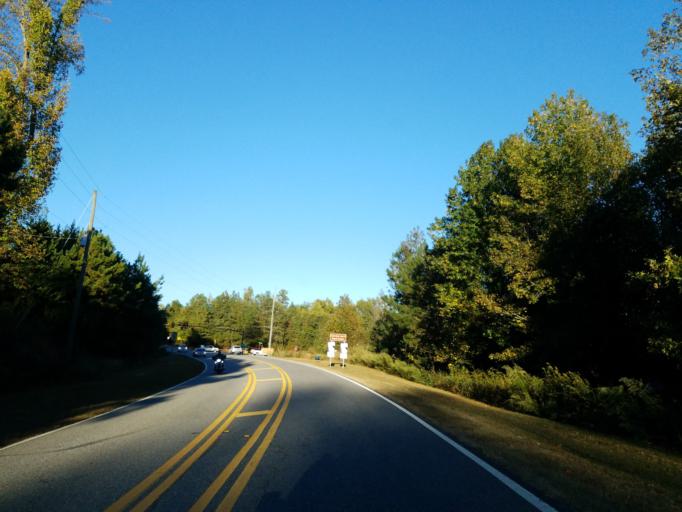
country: US
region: Georgia
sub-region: Dawson County
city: Dawsonville
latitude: 34.4105
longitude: -84.1077
